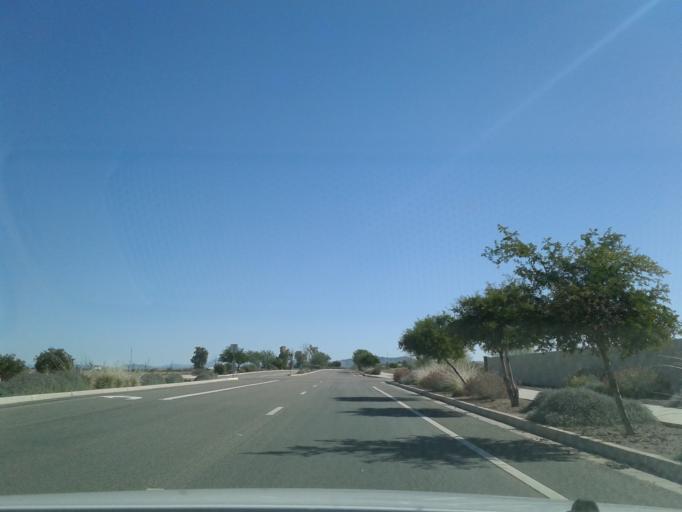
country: US
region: Arizona
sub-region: Pima County
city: Avra Valley
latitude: 32.5701
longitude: -111.3369
